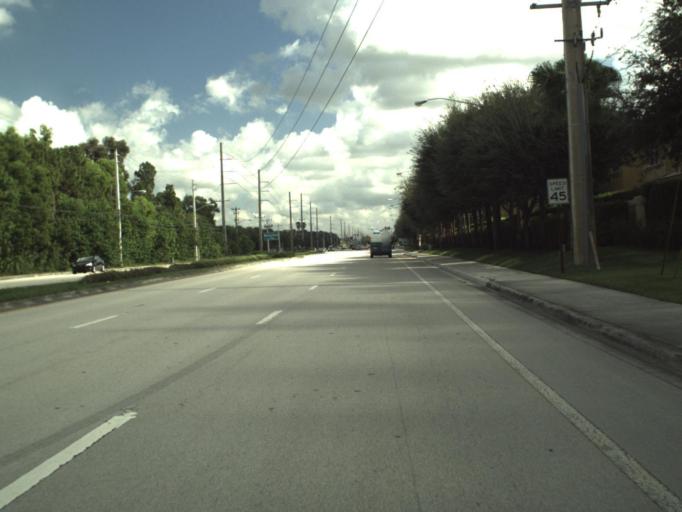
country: US
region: Florida
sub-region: Palm Beach County
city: Villages of Oriole
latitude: 26.5240
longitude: -80.1472
